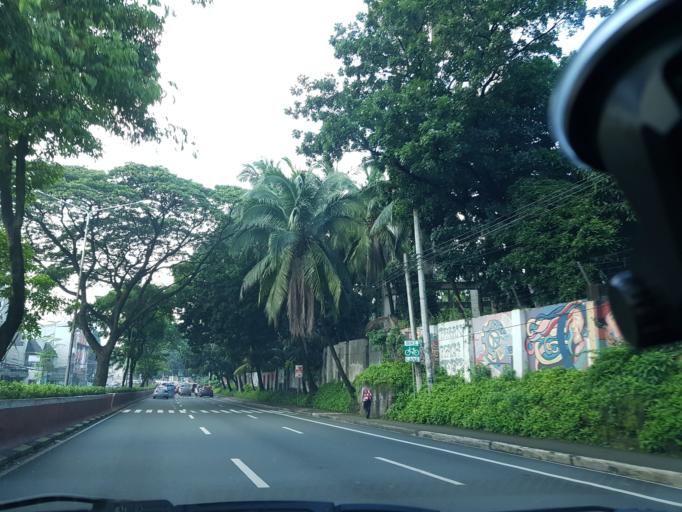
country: PH
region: Metro Manila
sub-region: Quezon City
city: Quezon City
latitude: 14.6357
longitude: 121.0545
